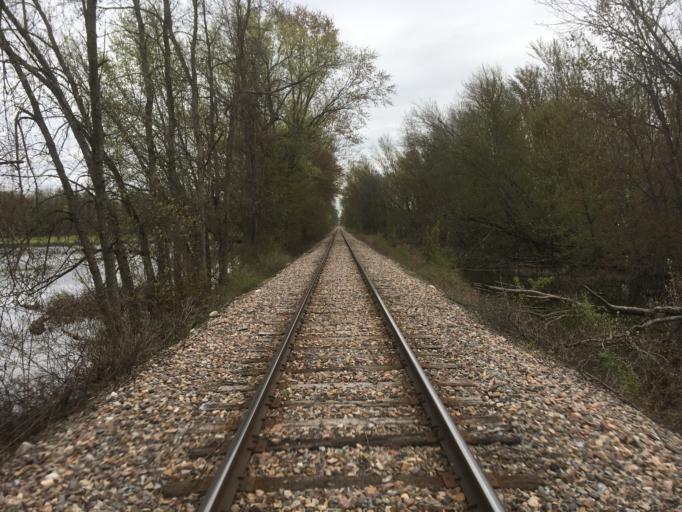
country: US
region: Vermont
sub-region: Addison County
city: Middlebury (village)
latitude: 43.9486
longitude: -73.1619
